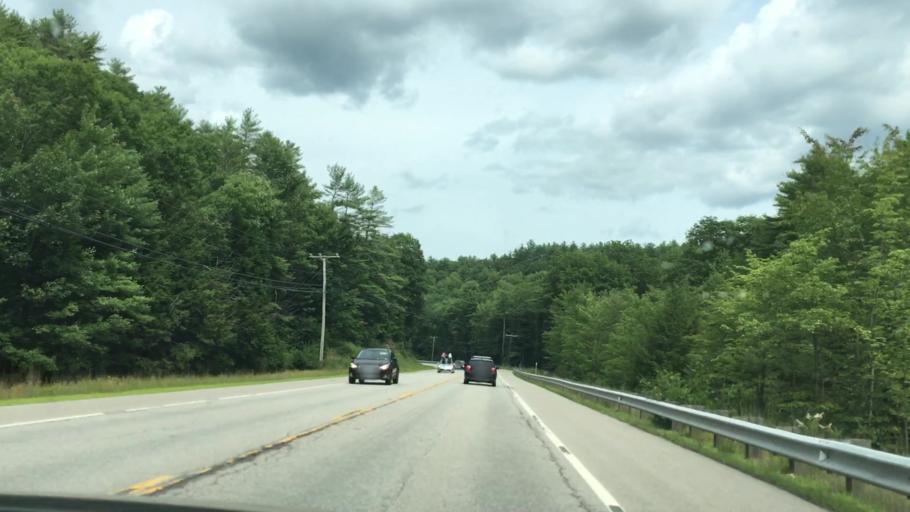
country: US
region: New Hampshire
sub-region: Hillsborough County
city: Peterborough
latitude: 42.8373
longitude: -71.9735
